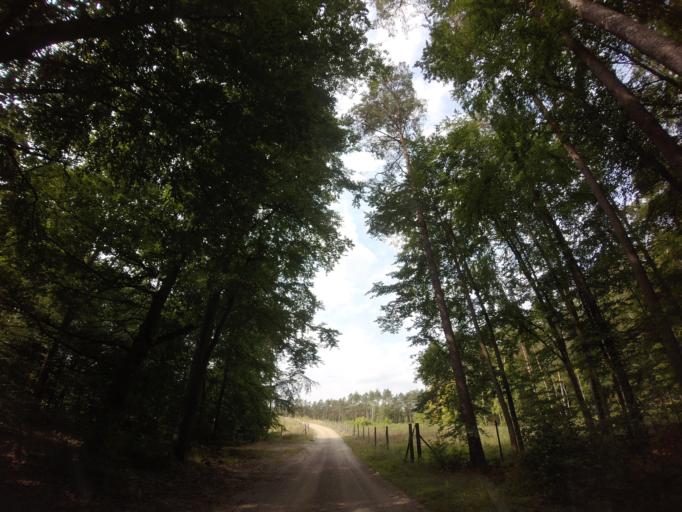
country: PL
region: West Pomeranian Voivodeship
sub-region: Powiat drawski
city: Drawsko Pomorskie
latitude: 53.4573
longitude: 15.7179
